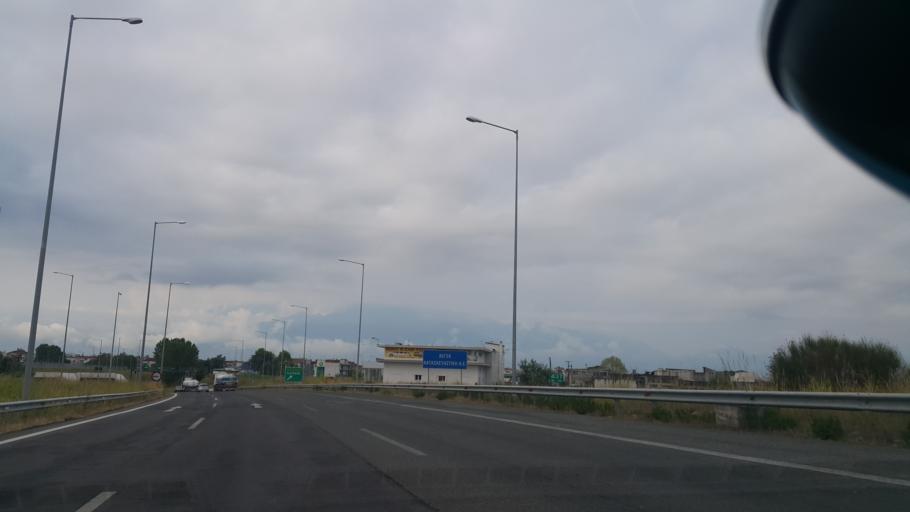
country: GR
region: Central Macedonia
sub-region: Nomos Pierias
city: Katerini
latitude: 40.2792
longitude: 22.5220
